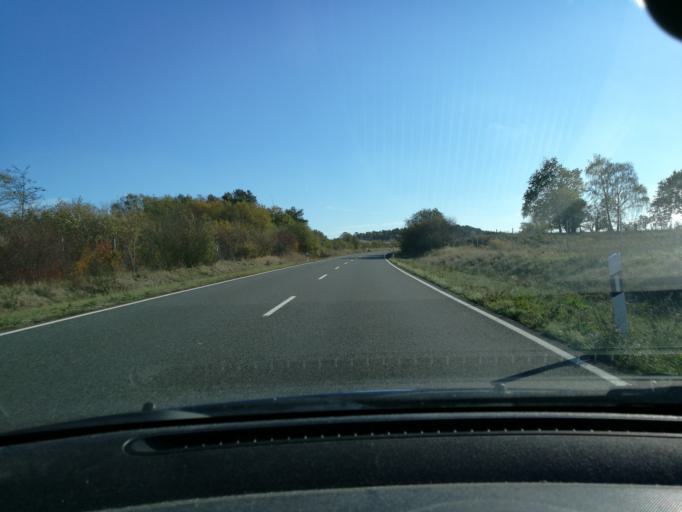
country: DE
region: Lower Saxony
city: Dahlem
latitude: 53.1919
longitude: 10.7546
